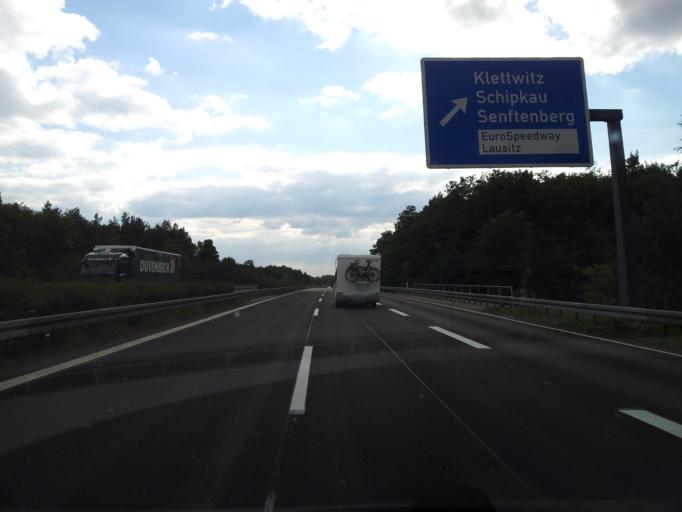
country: DE
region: Brandenburg
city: Schipkau
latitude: 51.5374
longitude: 13.9092
